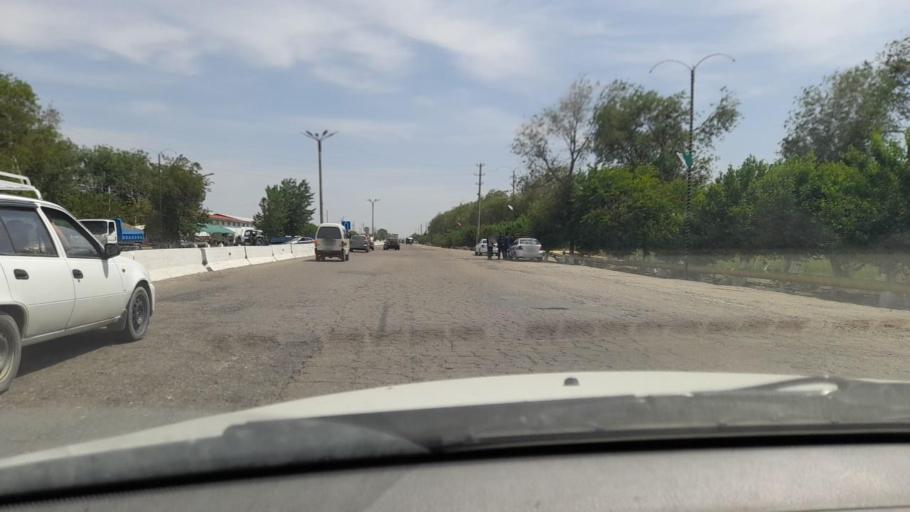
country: UZ
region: Bukhara
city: Ghijduwon
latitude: 40.0851
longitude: 64.6869
